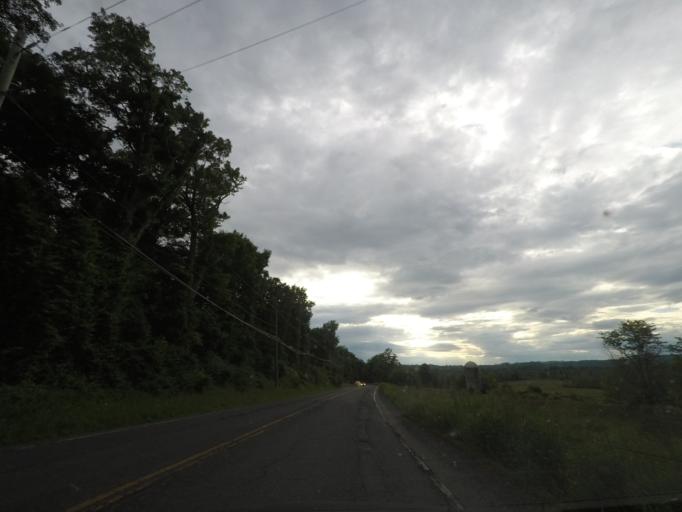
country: US
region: Connecticut
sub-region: Litchfield County
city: Canaan
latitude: 41.9558
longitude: -73.4801
